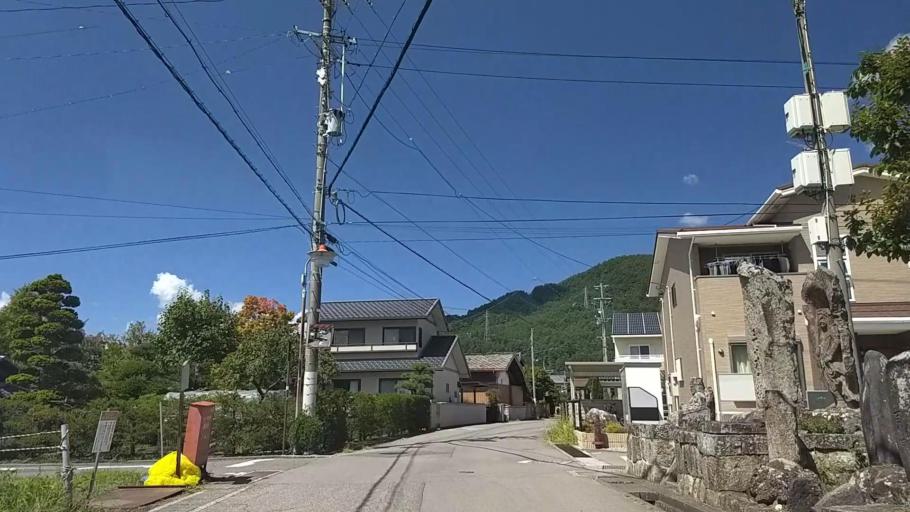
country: JP
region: Nagano
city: Chino
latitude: 35.9951
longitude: 138.1552
